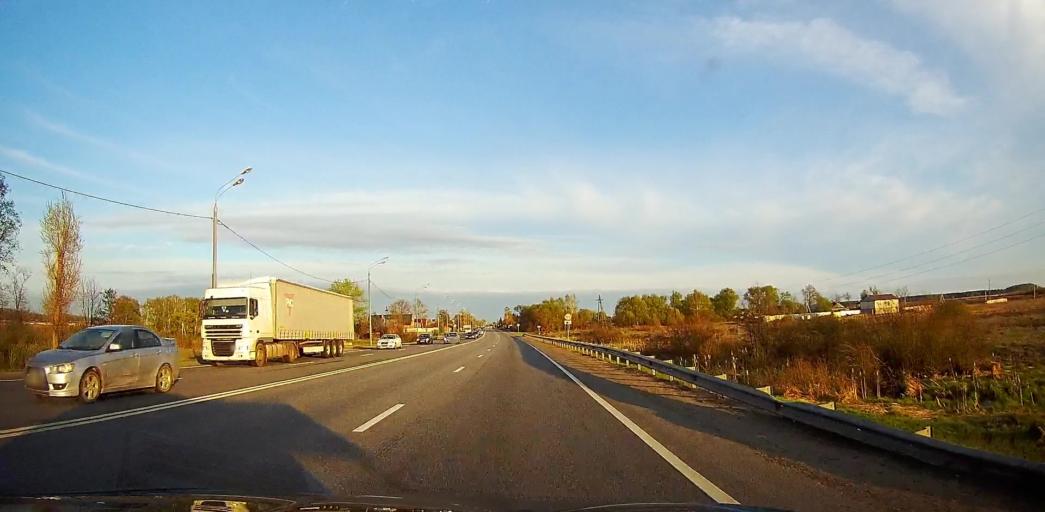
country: RU
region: Moskovskaya
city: Troitskoye
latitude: 55.2556
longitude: 38.5175
